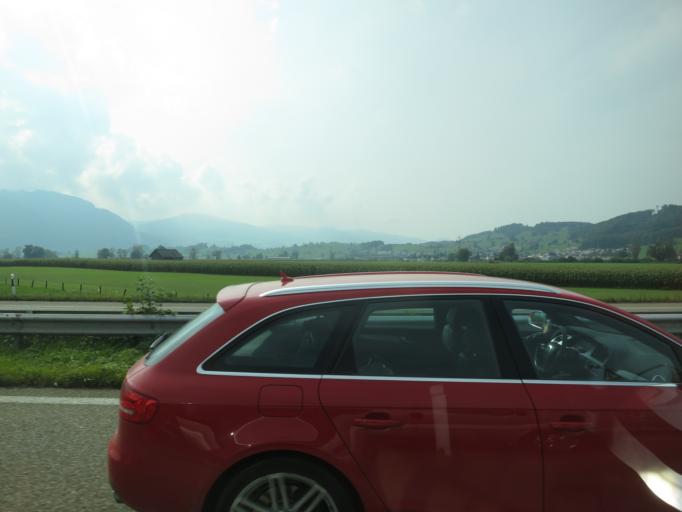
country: CH
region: Schwyz
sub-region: Bezirk March
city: Tuggen
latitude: 47.2052
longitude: 8.9653
